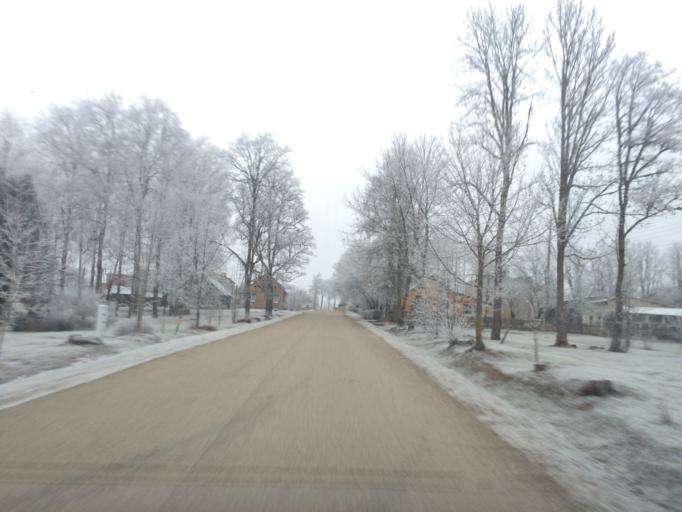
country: LV
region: Ludzas Rajons
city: Ludza
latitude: 56.6296
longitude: 27.5146
